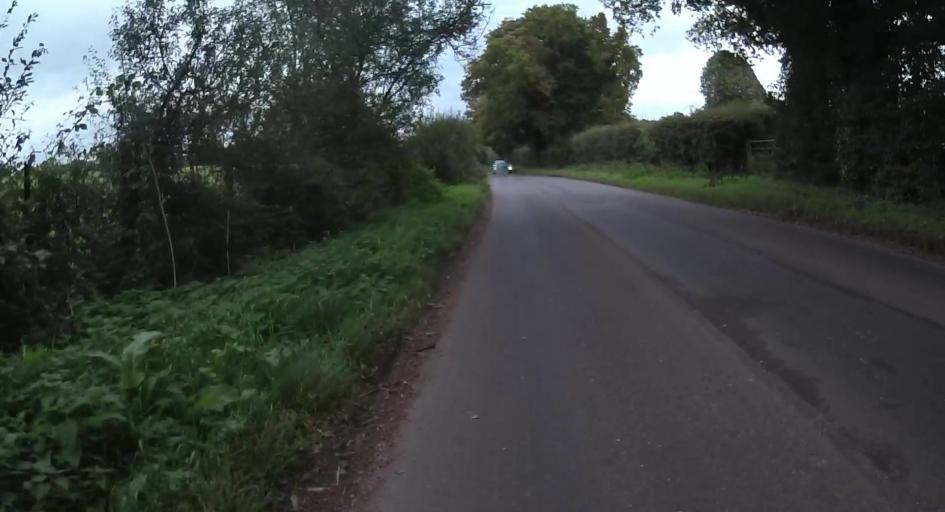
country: GB
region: England
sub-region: Hampshire
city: Four Marks
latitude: 51.0980
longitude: -1.0460
